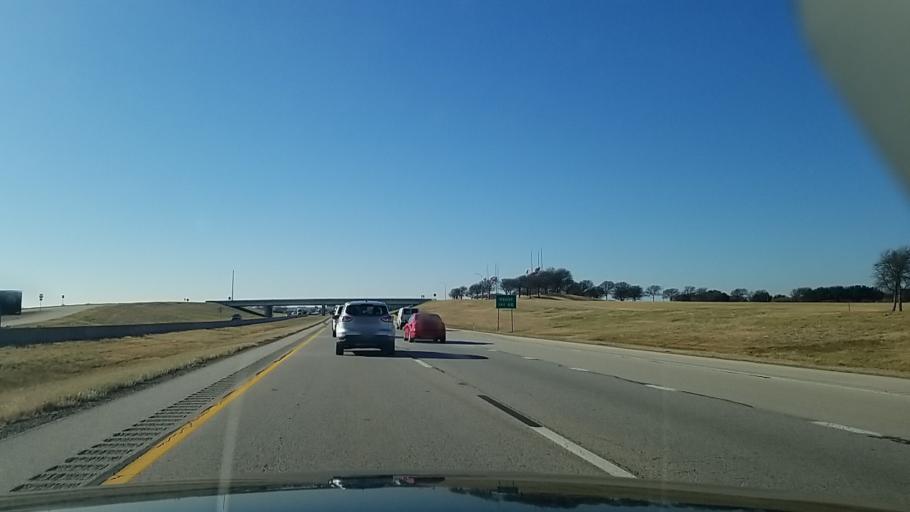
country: US
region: Texas
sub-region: Tarrant County
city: Haslet
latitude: 32.9888
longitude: -97.3013
